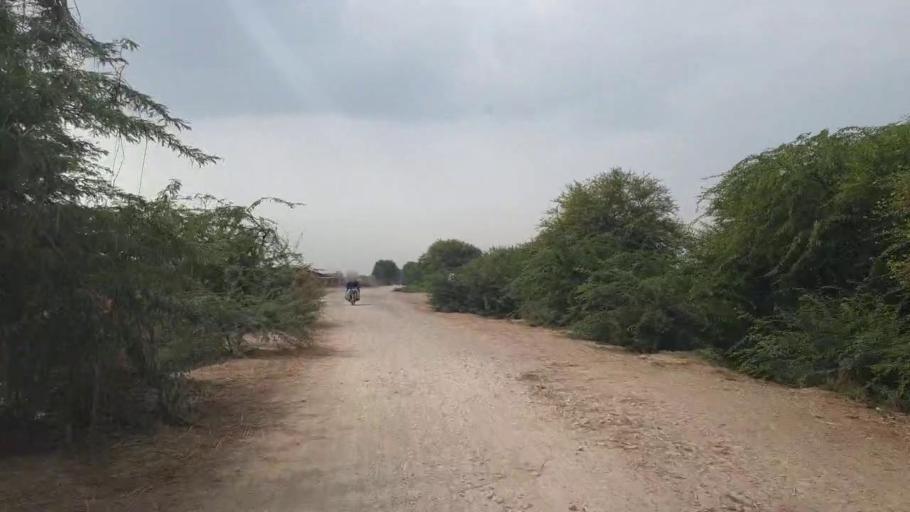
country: PK
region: Sindh
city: Talhar
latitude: 24.9184
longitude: 68.7775
